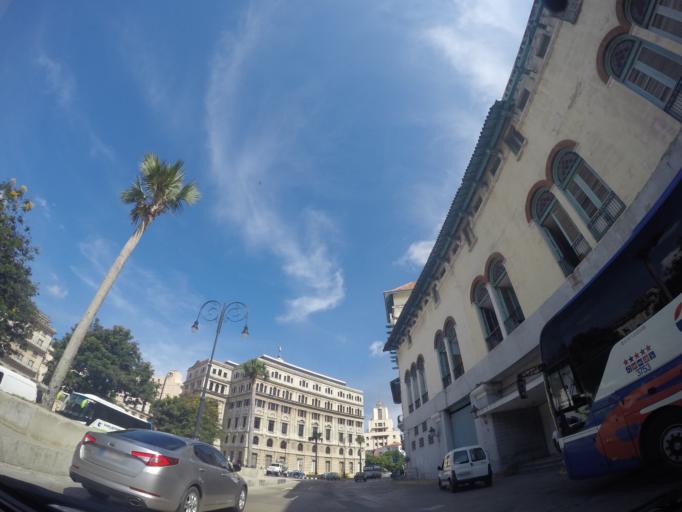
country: CU
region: La Habana
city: La Habana Vieja
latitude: 23.1372
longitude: -82.3480
